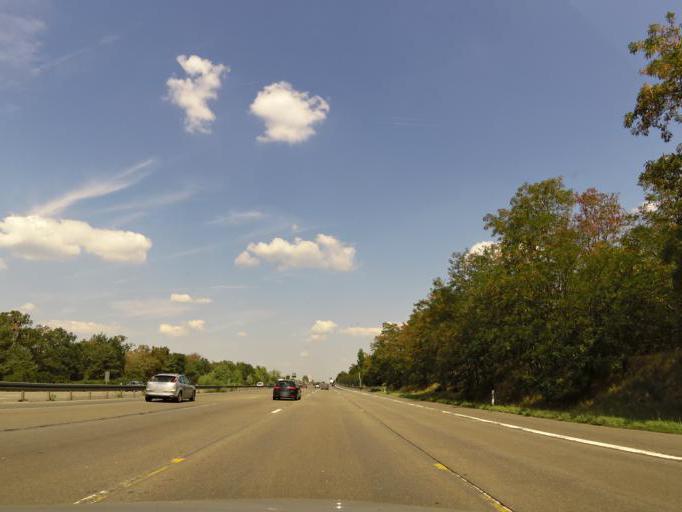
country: DE
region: Hesse
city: Weiterstadt
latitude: 49.8779
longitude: 8.6023
